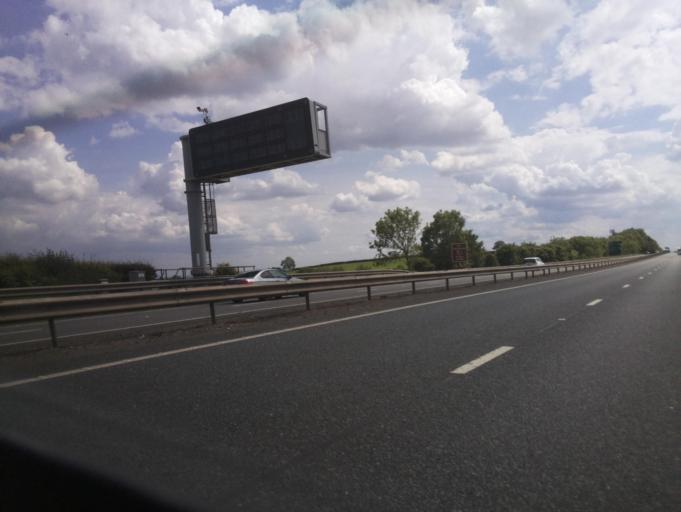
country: GB
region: England
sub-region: Hartlepool
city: Elwick
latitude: 54.6523
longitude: -1.3027
